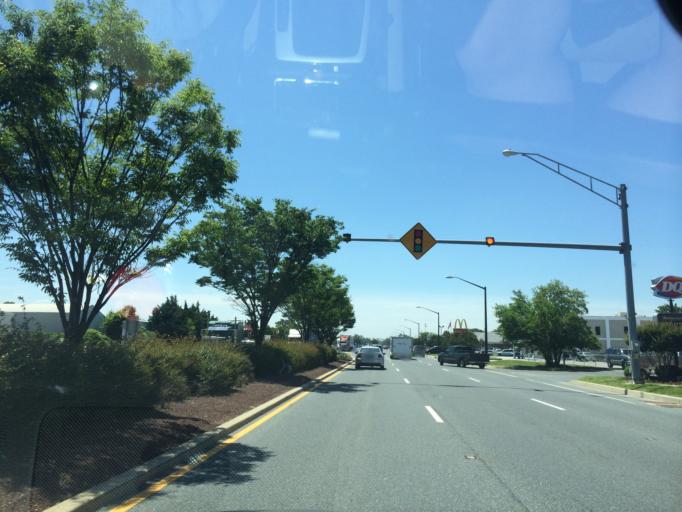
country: US
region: Maryland
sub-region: Talbot County
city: Easton
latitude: 38.7813
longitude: -76.0602
